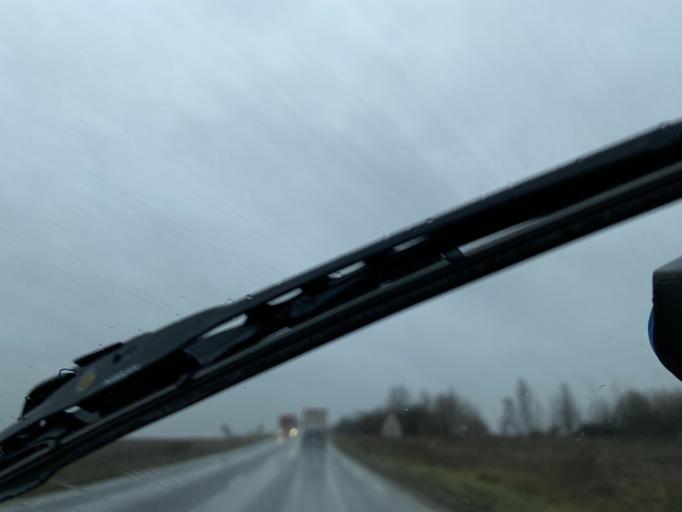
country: FR
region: Centre
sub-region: Departement d'Eure-et-Loir
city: Voves
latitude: 48.2830
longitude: 1.7282
